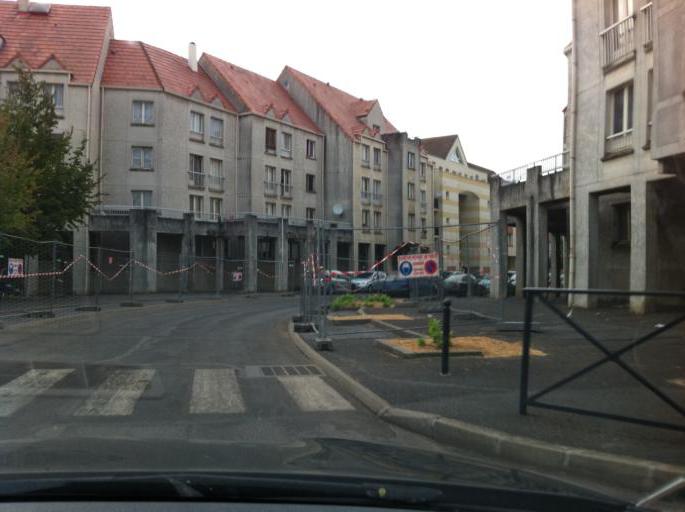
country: FR
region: Ile-de-France
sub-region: Departement de Seine-et-Marne
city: Moissy-Cramayel
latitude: 48.6246
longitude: 2.5812
